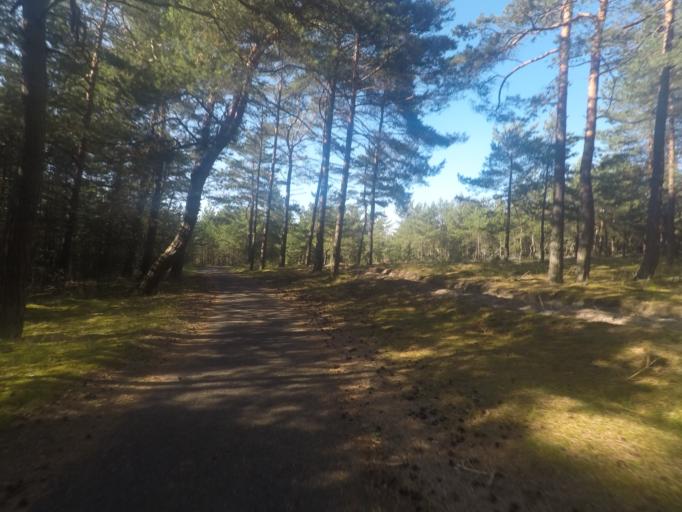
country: LT
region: Klaipedos apskritis
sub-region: Klaipeda
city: Klaipeda
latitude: 55.5654
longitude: 21.1120
